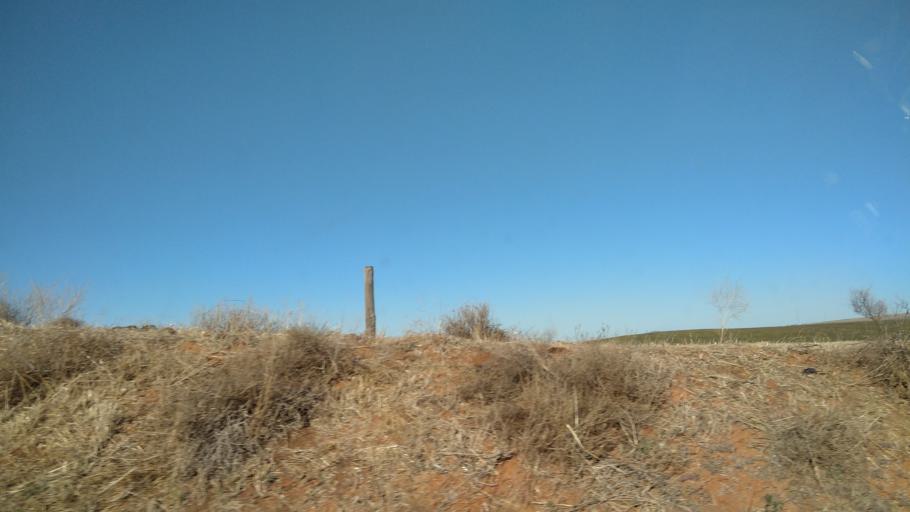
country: ZA
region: Western Cape
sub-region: West Coast District Municipality
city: Malmesbury
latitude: -33.4088
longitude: 18.6986
